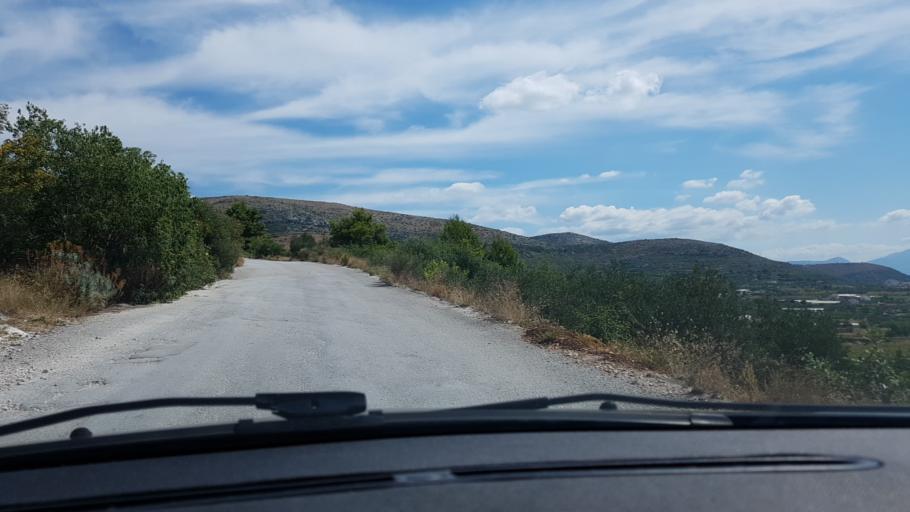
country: HR
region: Splitsko-Dalmatinska
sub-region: Grad Trogir
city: Trogir
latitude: 43.5250
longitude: 16.2271
